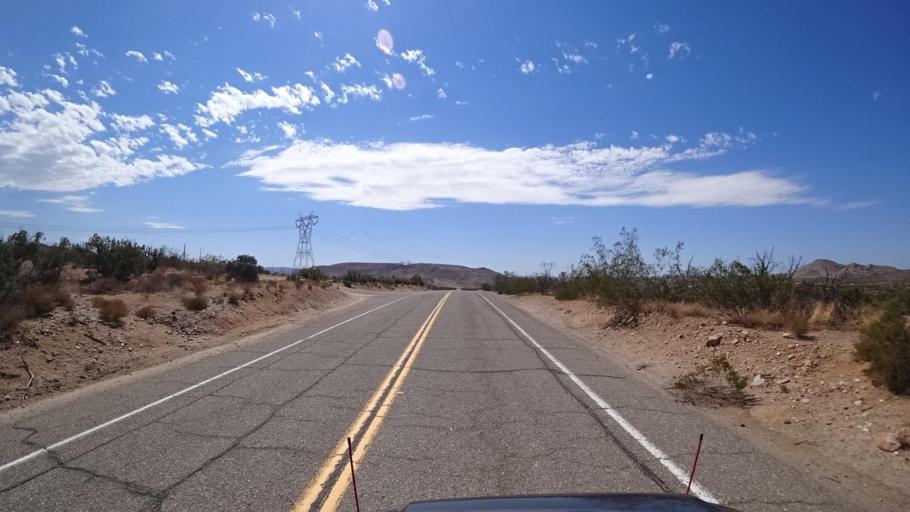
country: MX
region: Baja California
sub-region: Tecate
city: Cereso del Hongo
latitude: 32.6333
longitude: -116.1220
